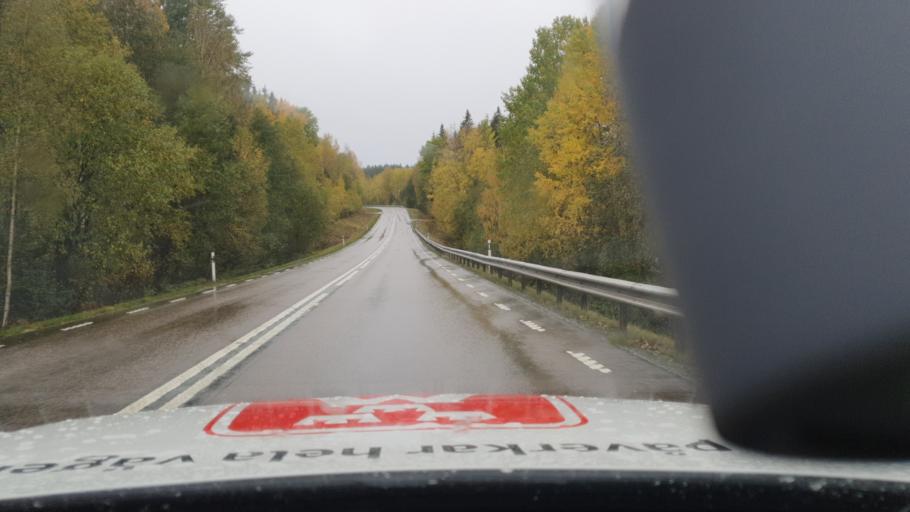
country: SE
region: Vaestra Goetaland
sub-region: Bengtsfors Kommun
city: Billingsfors
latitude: 58.9402
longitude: 12.1159
